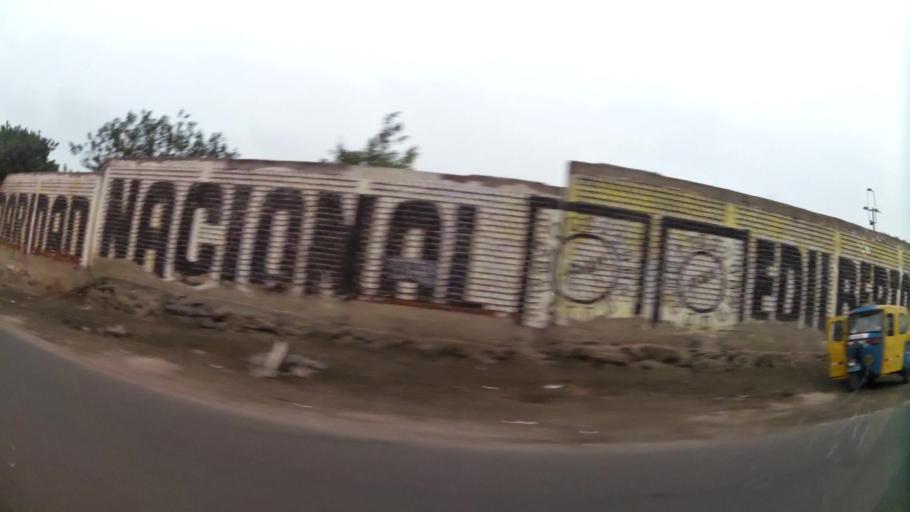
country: PE
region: Lima
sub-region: Lima
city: Surco
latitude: -12.1632
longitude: -76.9711
